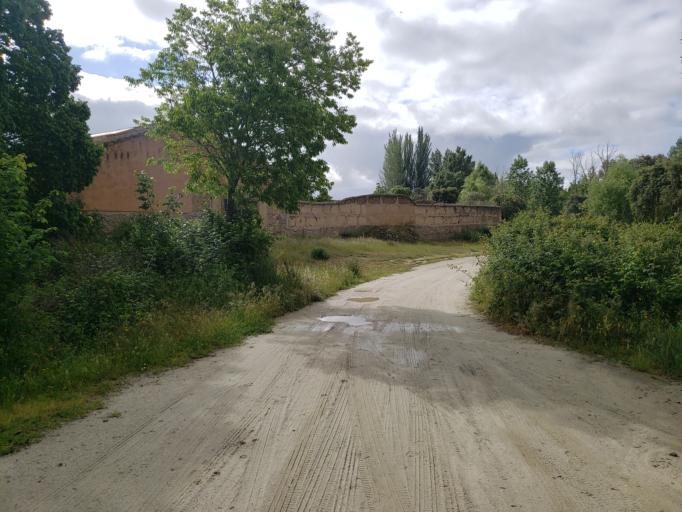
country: ES
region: Extremadura
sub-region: Provincia de Caceres
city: Malpartida de Caceres
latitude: 39.4224
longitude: -6.5053
